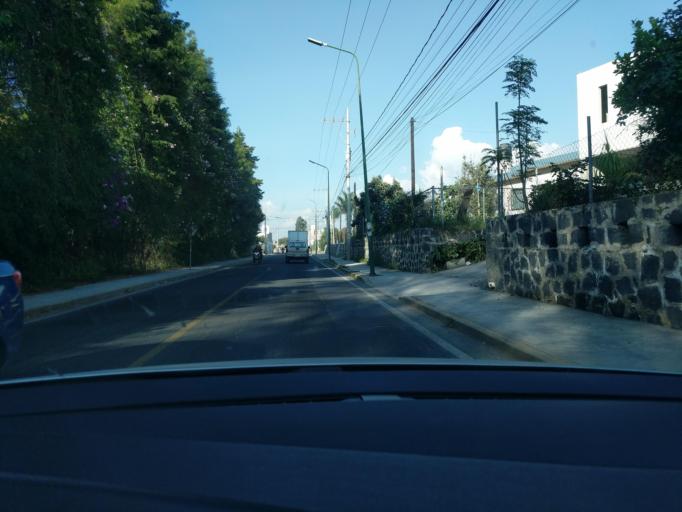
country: MX
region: Puebla
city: San Andres Cholula
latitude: 19.0337
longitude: -98.3177
